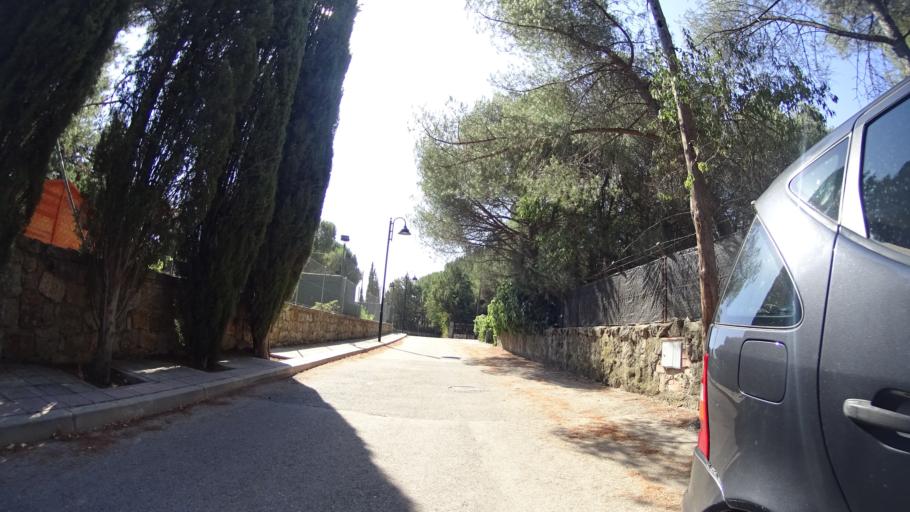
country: ES
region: Madrid
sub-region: Provincia de Madrid
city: Galapagar
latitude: 40.5942
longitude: -3.9824
